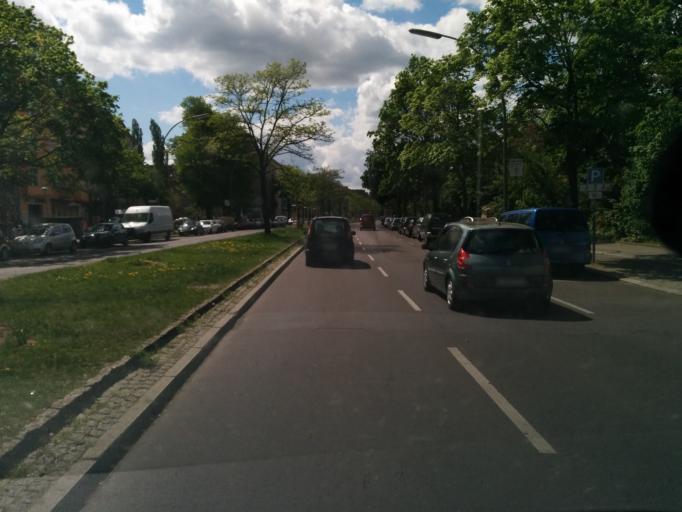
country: DE
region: Berlin
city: Wilhelmstadt
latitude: 52.5252
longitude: 13.1935
